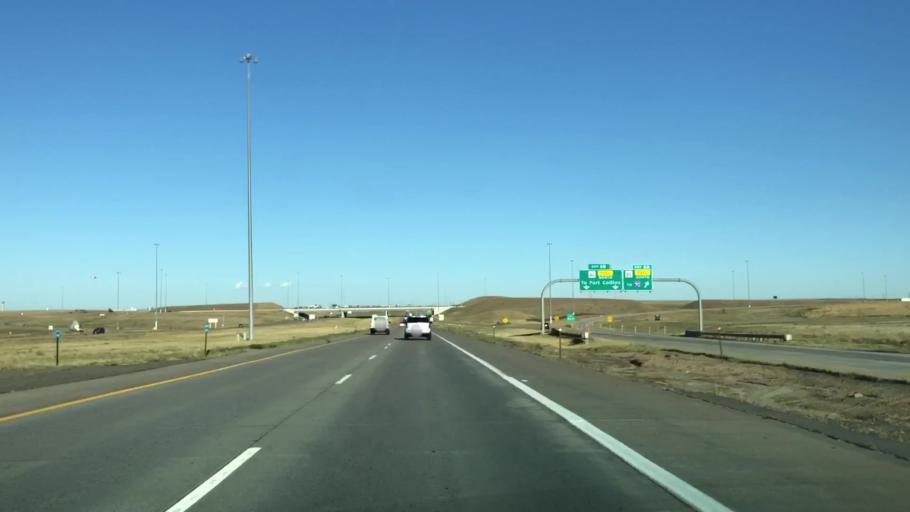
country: US
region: Colorado
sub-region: Adams County
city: Aurora
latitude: 39.8339
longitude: -104.7569
